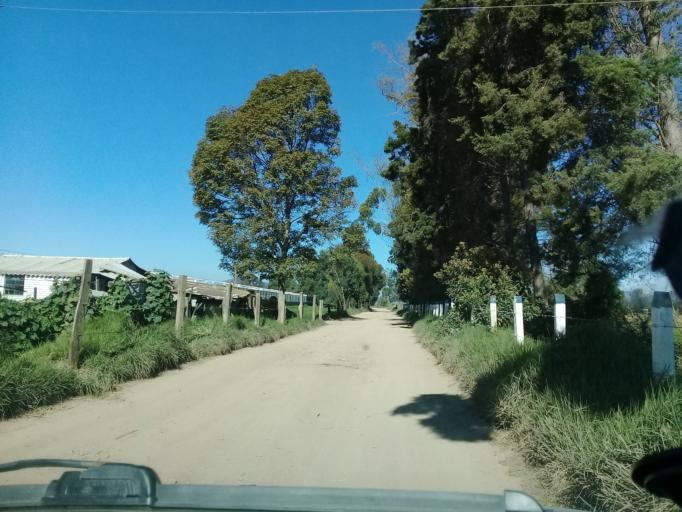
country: CO
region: Cundinamarca
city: Madrid
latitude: 4.7532
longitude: -74.2414
